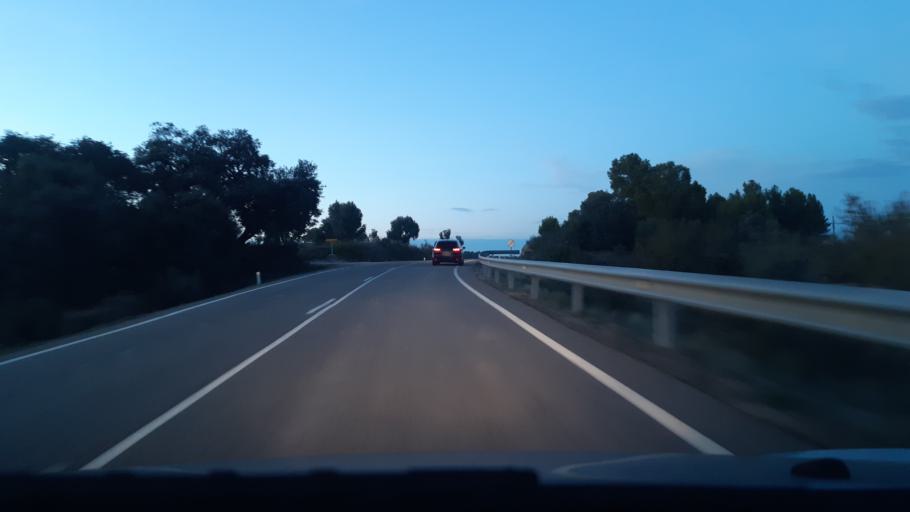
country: ES
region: Aragon
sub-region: Provincia de Teruel
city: Calaceite
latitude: 40.9857
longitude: 0.1993
